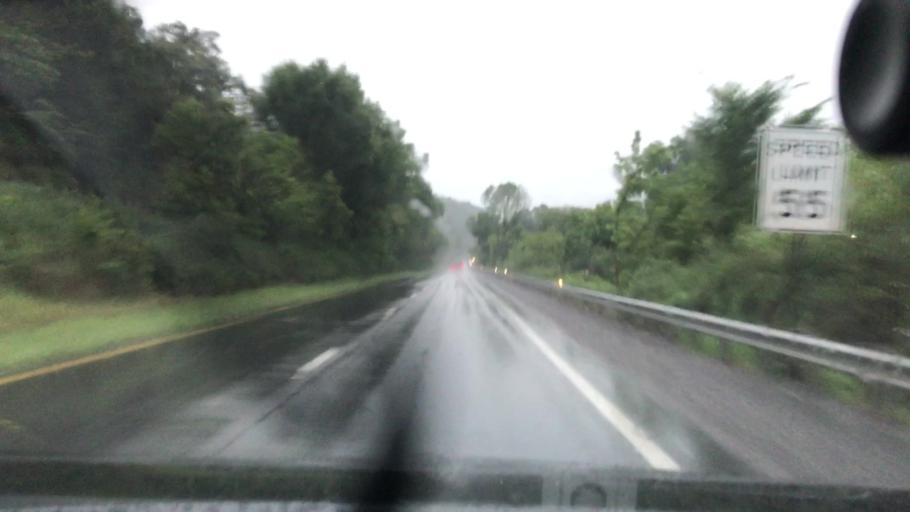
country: US
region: Virginia
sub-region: Giles County
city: Narrows
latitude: 37.3787
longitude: -80.8226
